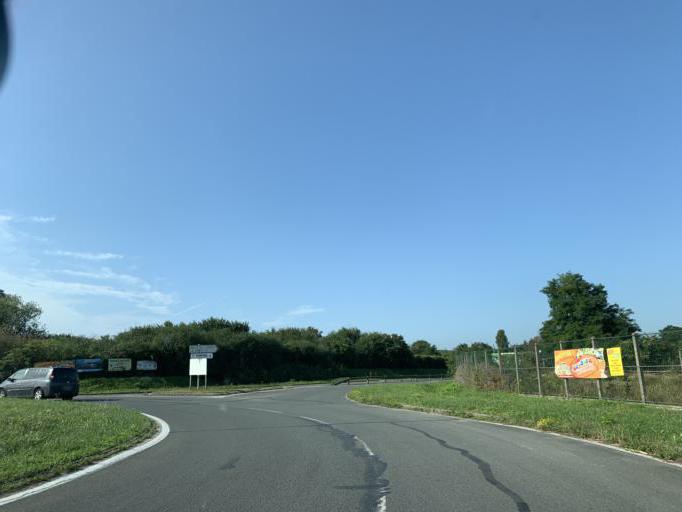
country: FR
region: Ile-de-France
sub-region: Departement de Seine-et-Marne
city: Annet-sur-Marne
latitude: 48.9185
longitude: 2.7441
